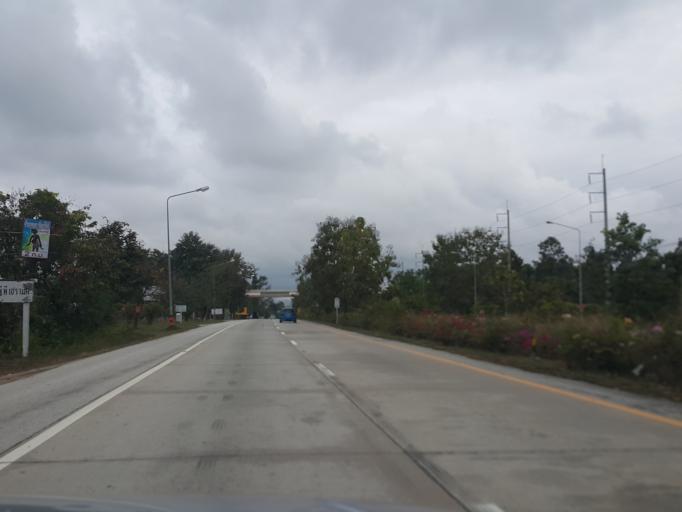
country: TH
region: Lampang
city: Hang Chat
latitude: 18.3124
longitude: 99.3860
